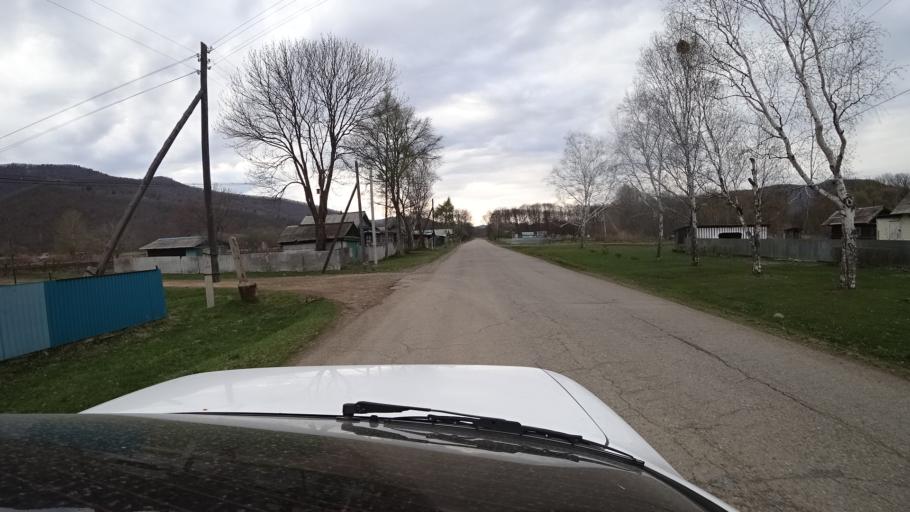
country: RU
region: Primorskiy
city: Novopokrovka
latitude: 45.1453
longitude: 134.3843
